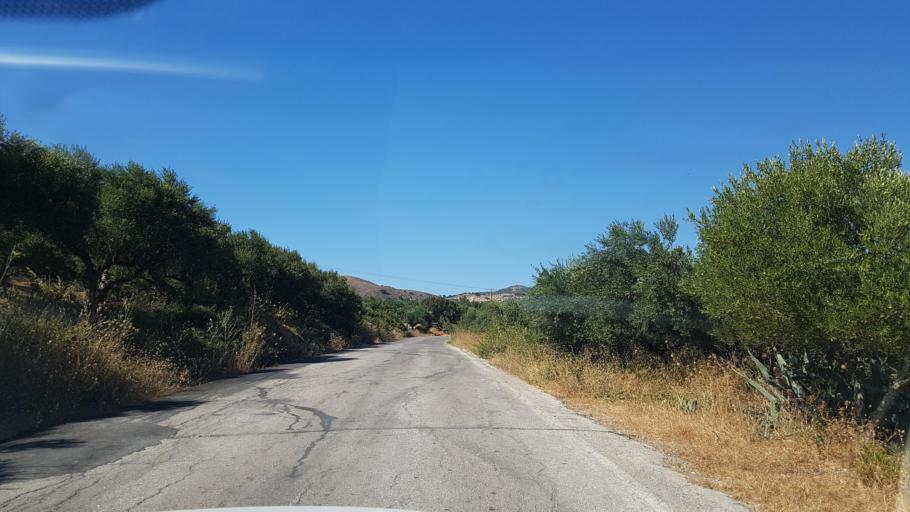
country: GR
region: Crete
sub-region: Nomos Chanias
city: Kissamos
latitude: 35.4998
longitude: 23.7229
